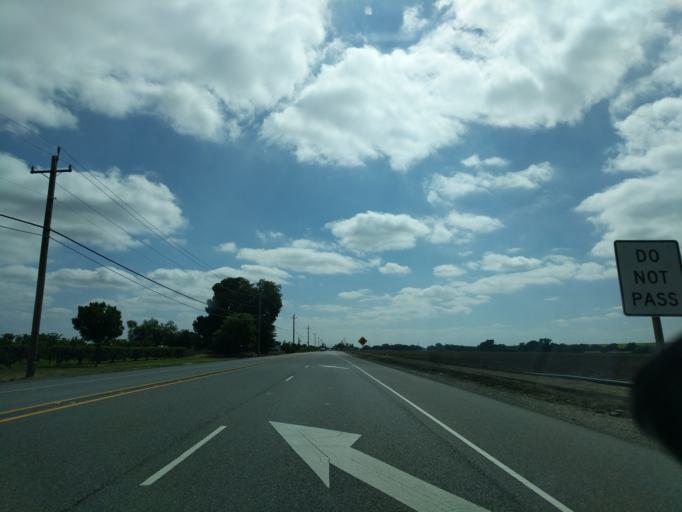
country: US
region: California
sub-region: Contra Costa County
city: Brentwood
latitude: 37.8963
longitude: -121.7068
